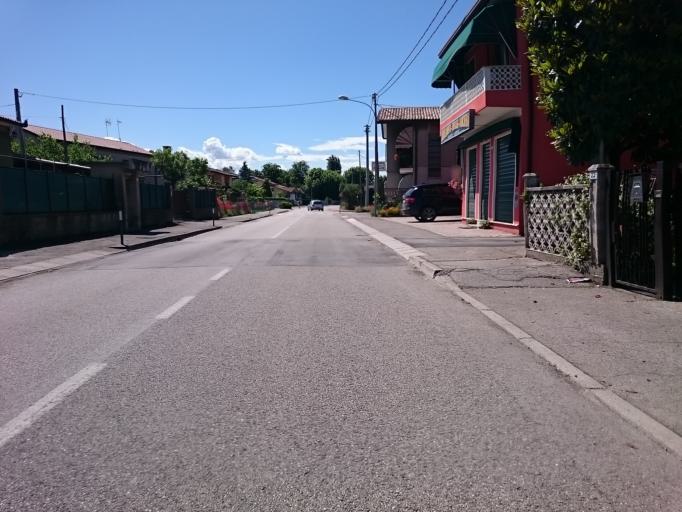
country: IT
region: Veneto
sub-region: Provincia di Padova
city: Vallonga
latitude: 45.2720
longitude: 12.0801
